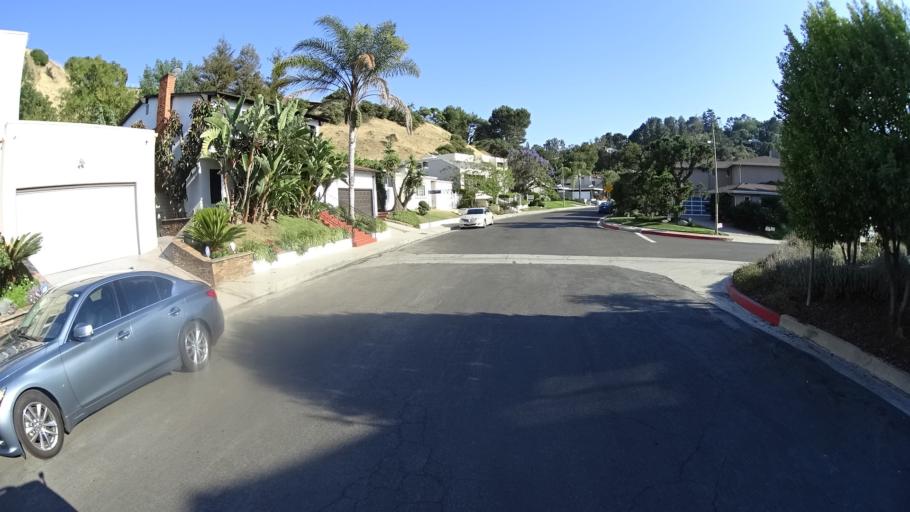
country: US
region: California
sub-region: Los Angeles County
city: Universal City
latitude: 34.1264
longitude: -118.3757
